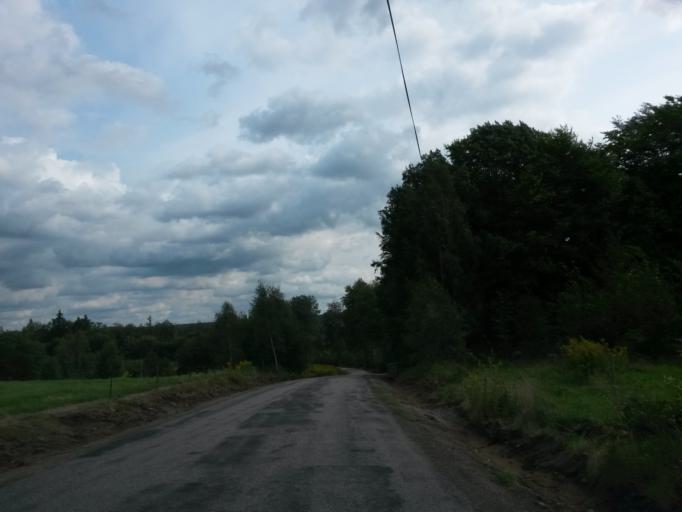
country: SE
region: Kronoberg
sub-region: Vaxjo Kommun
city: Vaexjoe
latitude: 56.9004
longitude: 14.8700
